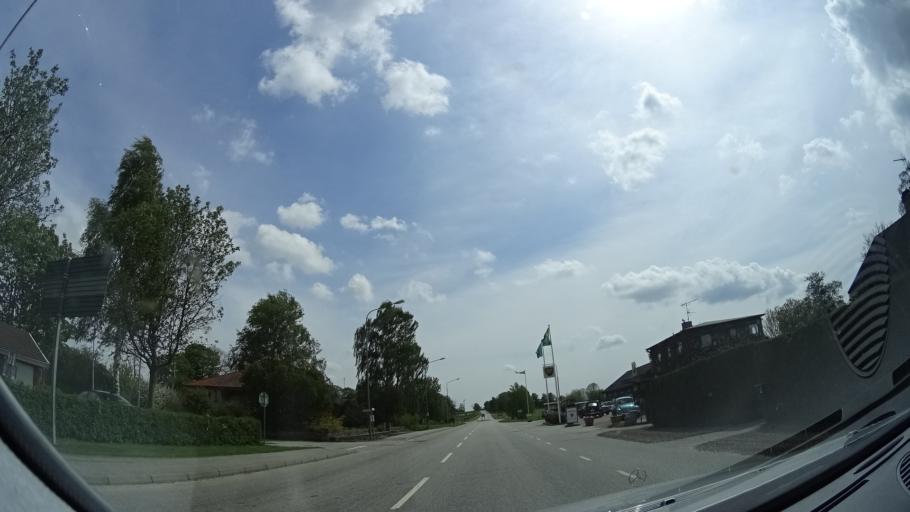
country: SE
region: Skane
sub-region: Hoors Kommun
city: Loberod
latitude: 55.7158
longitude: 13.5299
